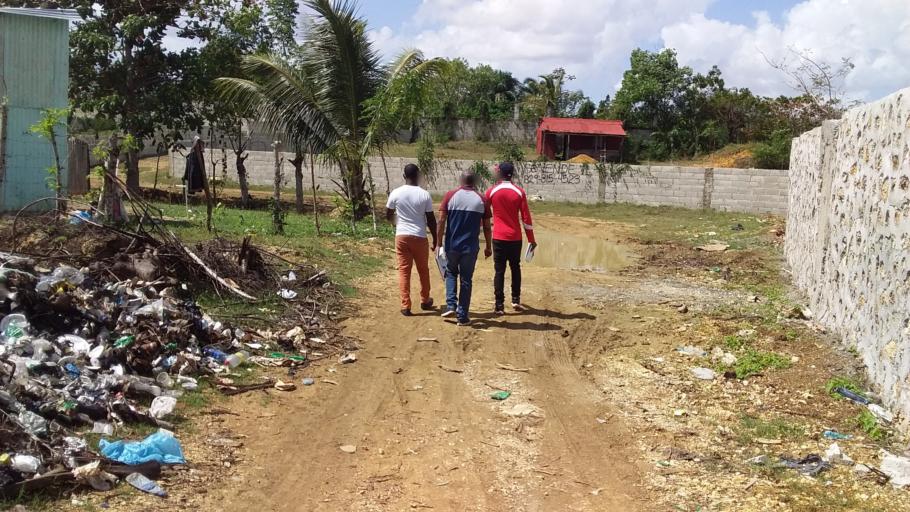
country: DO
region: Santo Domingo
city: Guerra
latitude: 18.5647
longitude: -69.7810
